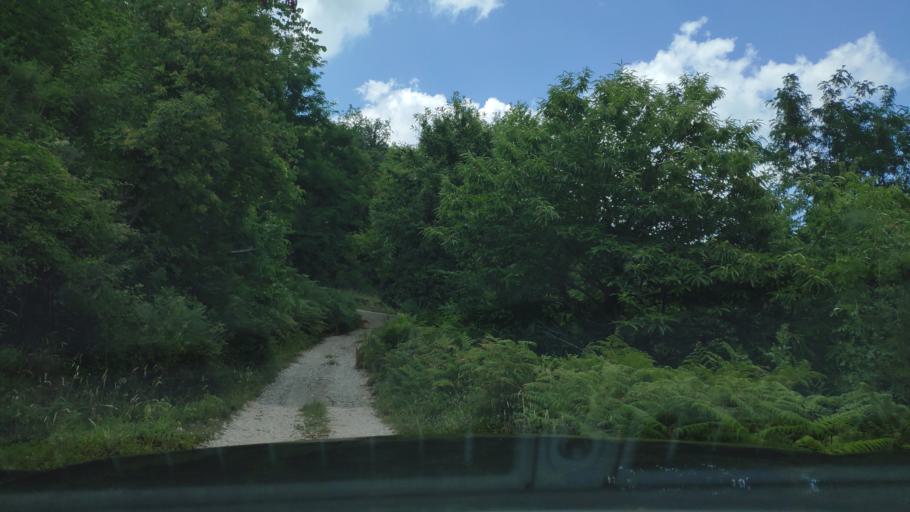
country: GR
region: Epirus
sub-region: Nomos Artas
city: Agios Dimitrios
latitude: 39.3187
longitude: 21.0005
